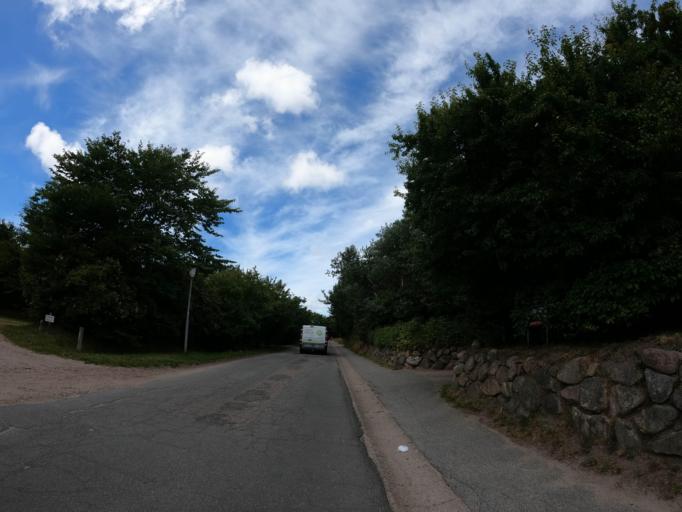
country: DE
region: Schleswig-Holstein
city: Keitum
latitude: 54.9011
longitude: 8.3664
